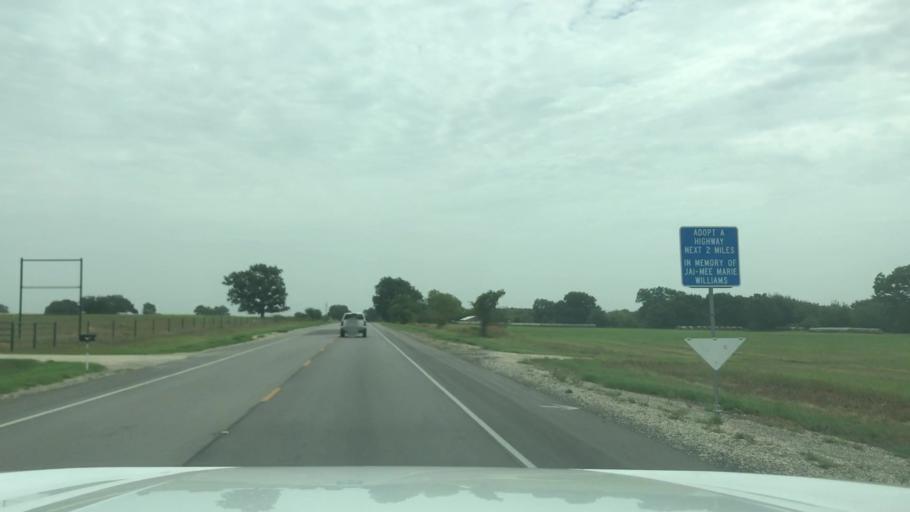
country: US
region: Texas
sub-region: Erath County
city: Dublin
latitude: 32.0901
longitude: -98.2845
